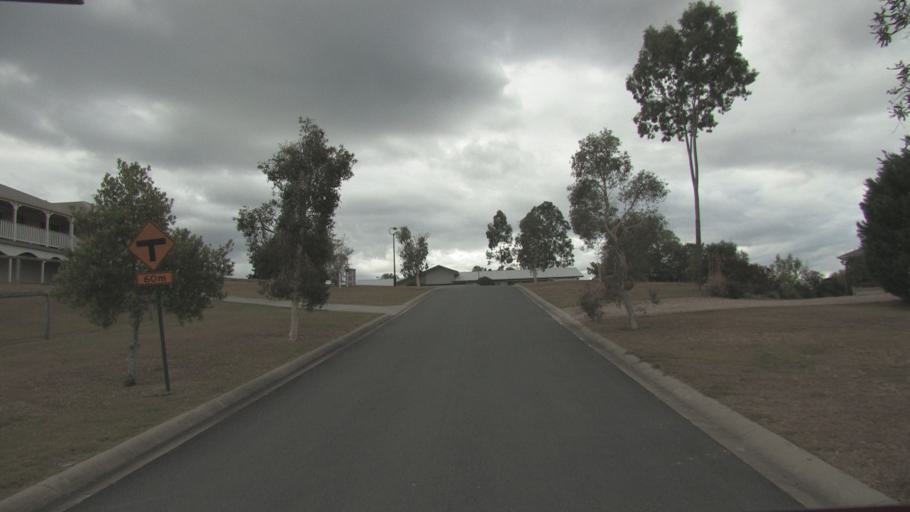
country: AU
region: Queensland
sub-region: Logan
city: Cedar Vale
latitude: -27.8688
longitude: 153.0791
